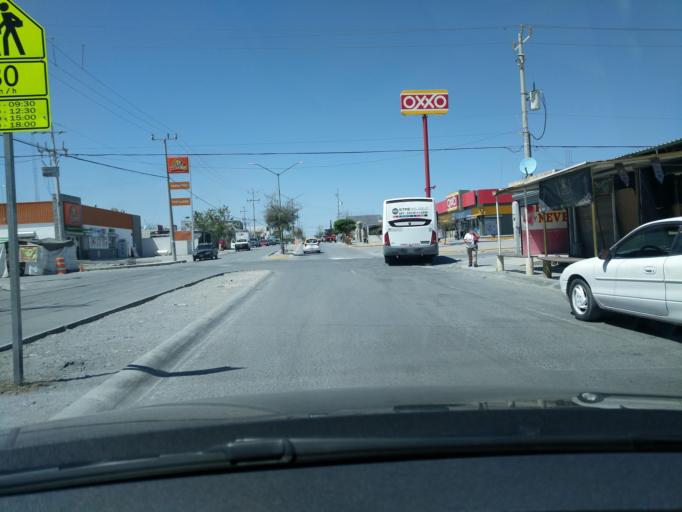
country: MX
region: Nuevo Leon
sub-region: Pesqueria
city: Colinas del Aeropuerto
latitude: 25.8239
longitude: -100.1207
